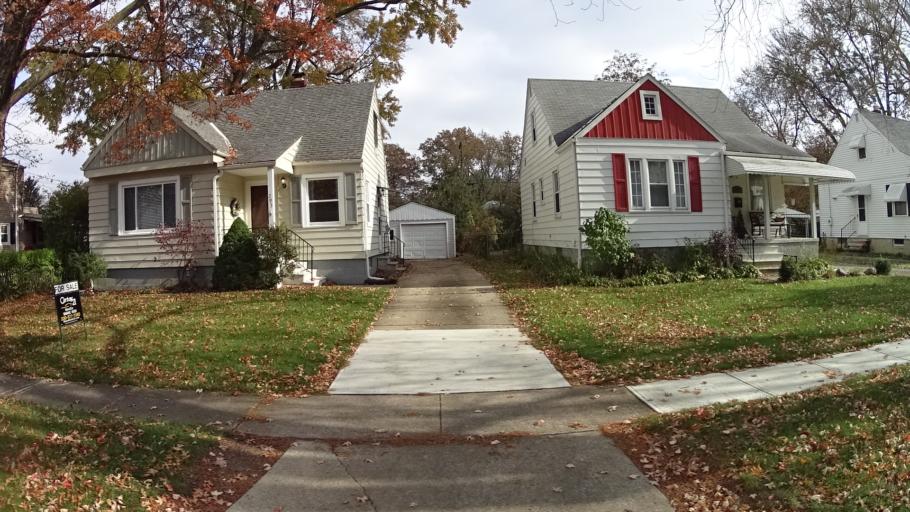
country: US
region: Ohio
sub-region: Lorain County
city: Elyria
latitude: 41.3810
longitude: -82.0882
